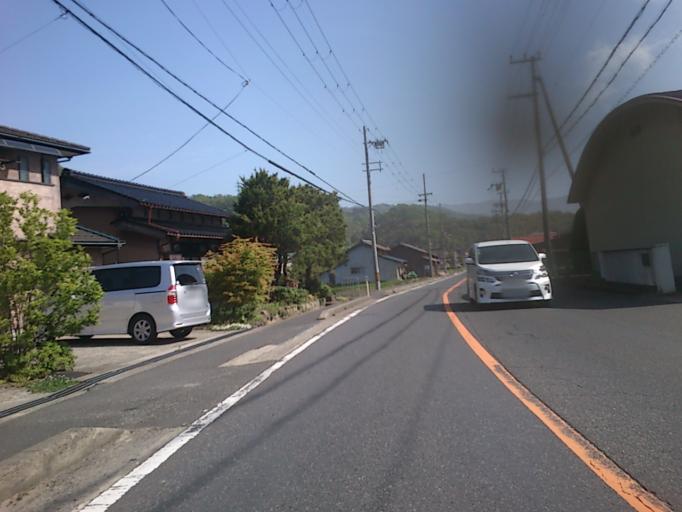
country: JP
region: Kyoto
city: Miyazu
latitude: 35.5568
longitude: 135.1393
